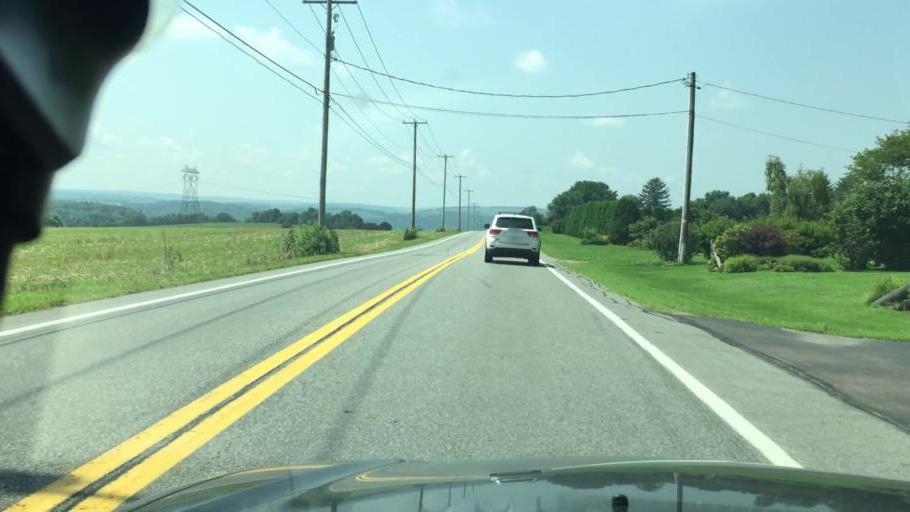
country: US
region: Pennsylvania
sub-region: Columbia County
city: Catawissa
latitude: 40.9239
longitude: -76.4641
